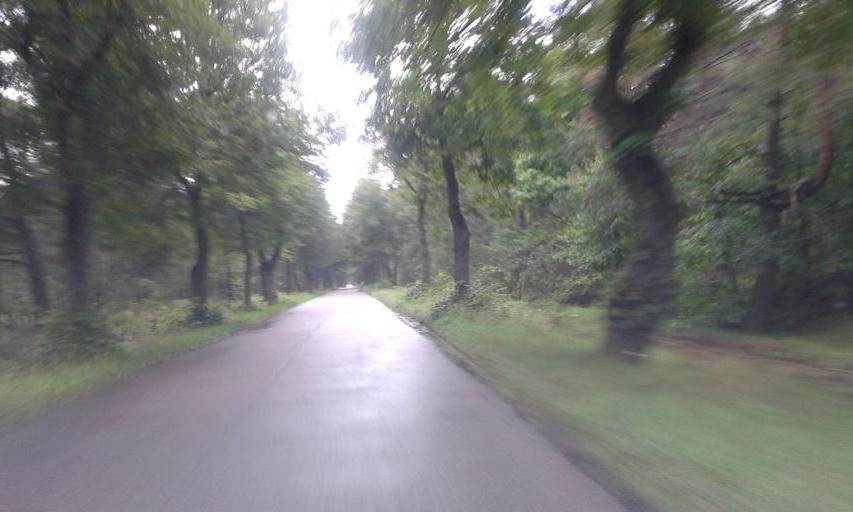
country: PL
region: West Pomeranian Voivodeship
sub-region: Powiat szczecinecki
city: Borne Sulinowo
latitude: 53.5044
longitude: 16.4986
